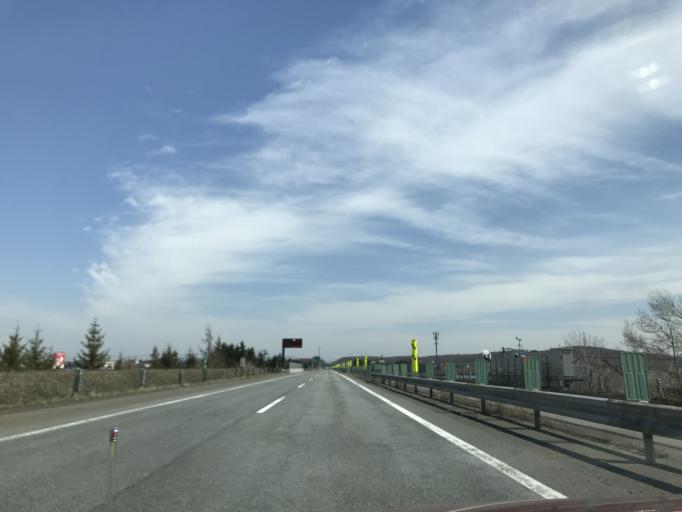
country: JP
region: Hokkaido
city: Iwamizawa
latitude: 43.1706
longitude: 141.7589
